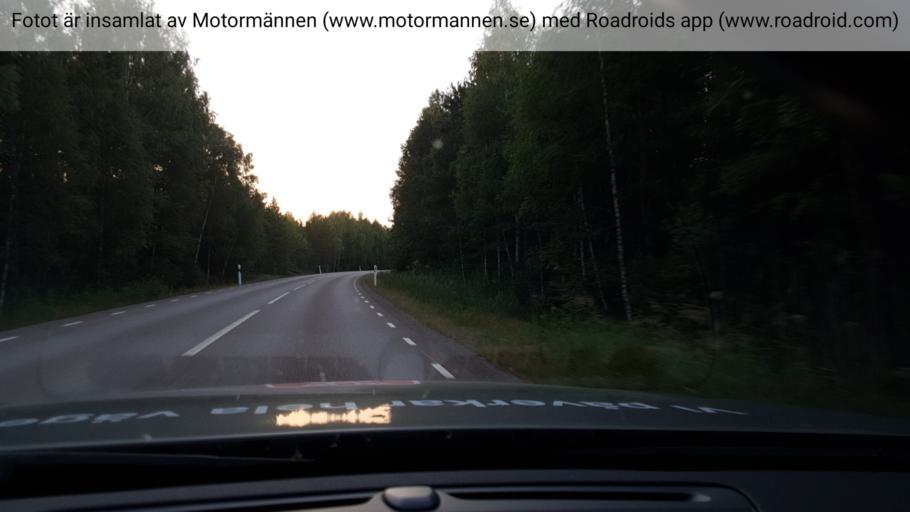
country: SE
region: Uppsala
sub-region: Heby Kommun
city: OEstervala
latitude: 60.0409
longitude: 17.2430
